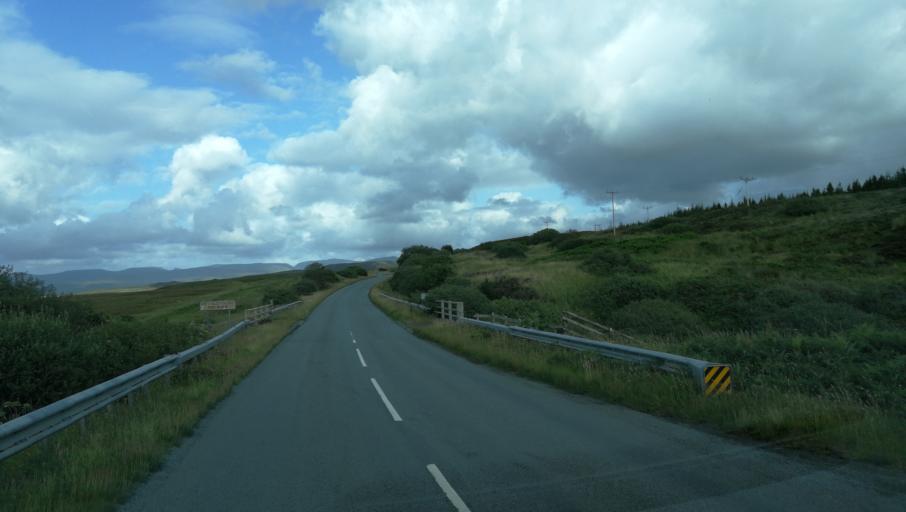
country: GB
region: Scotland
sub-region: Highland
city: Isle of Skye
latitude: 57.4707
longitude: -6.4720
